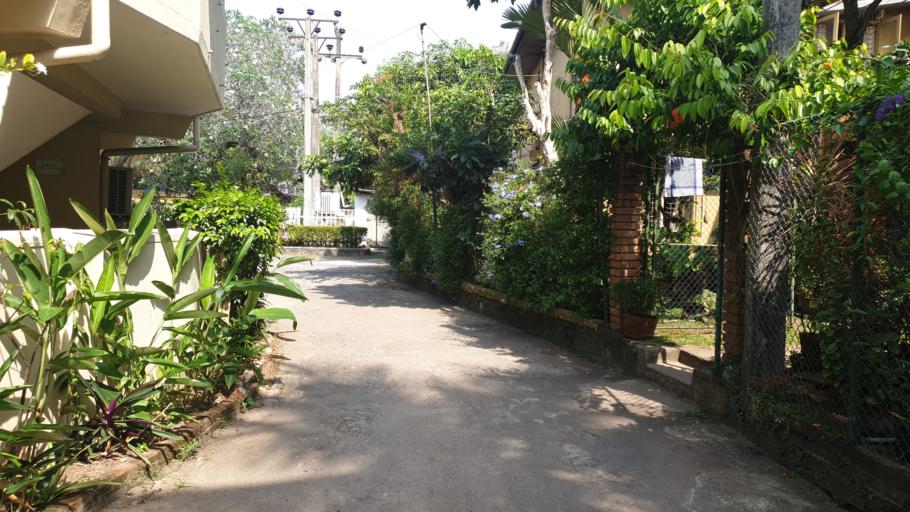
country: LK
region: Western
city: Moratuwa
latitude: 6.7888
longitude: 79.8893
